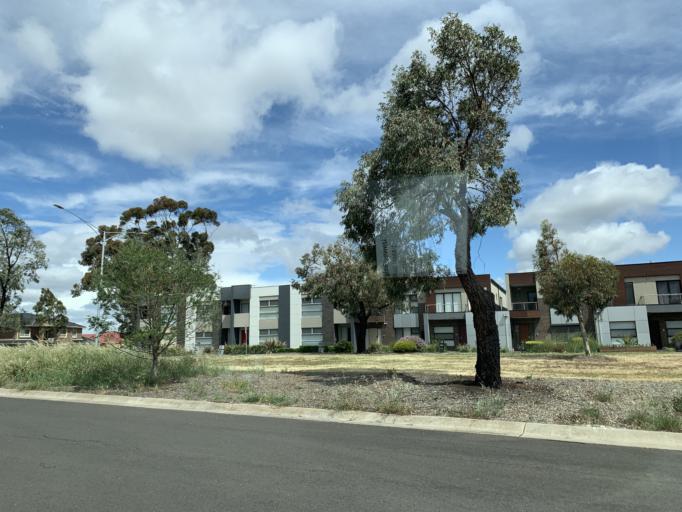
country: AU
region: Victoria
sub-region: Brimbank
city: Cairnlea
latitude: -37.7603
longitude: 144.7906
